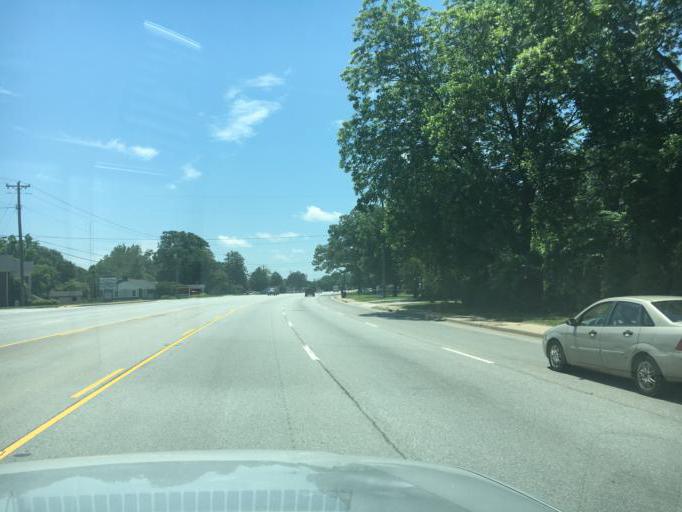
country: US
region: South Carolina
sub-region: Greenville County
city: Berea
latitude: 34.9000
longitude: -82.4637
